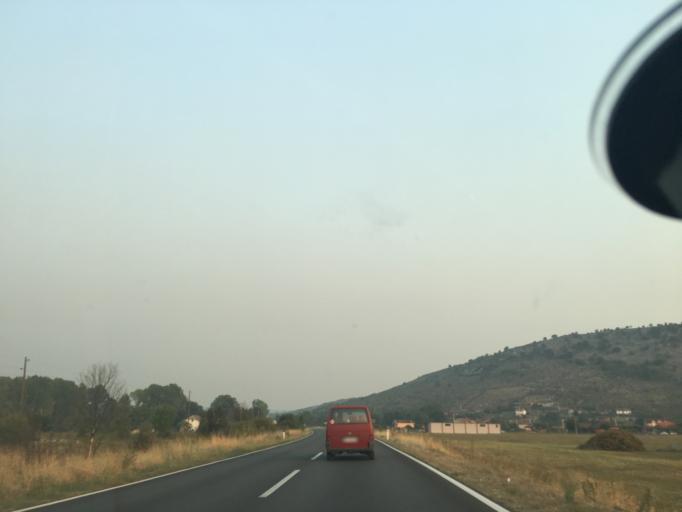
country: ME
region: Danilovgrad
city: Danilovgrad
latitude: 42.5118
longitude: 19.1285
